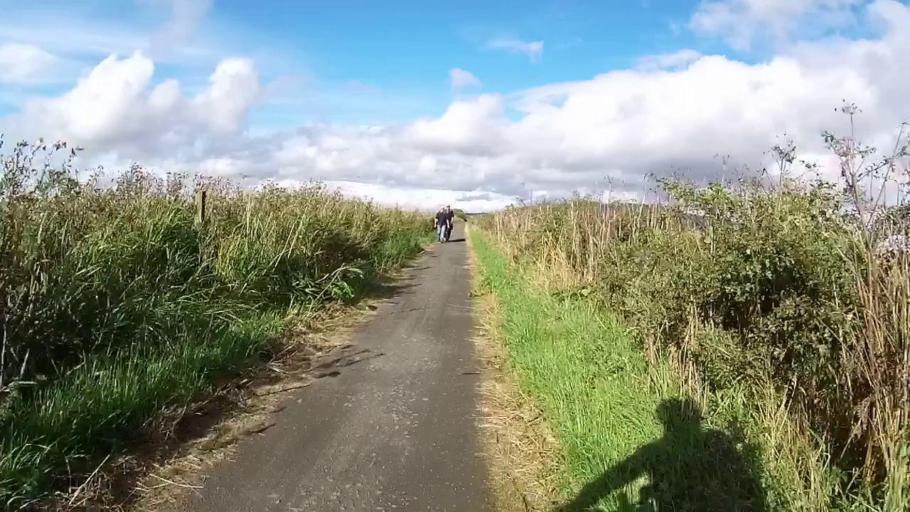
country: GB
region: Scotland
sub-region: Perth and Kinross
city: Kinross
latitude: 56.1788
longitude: -3.3875
